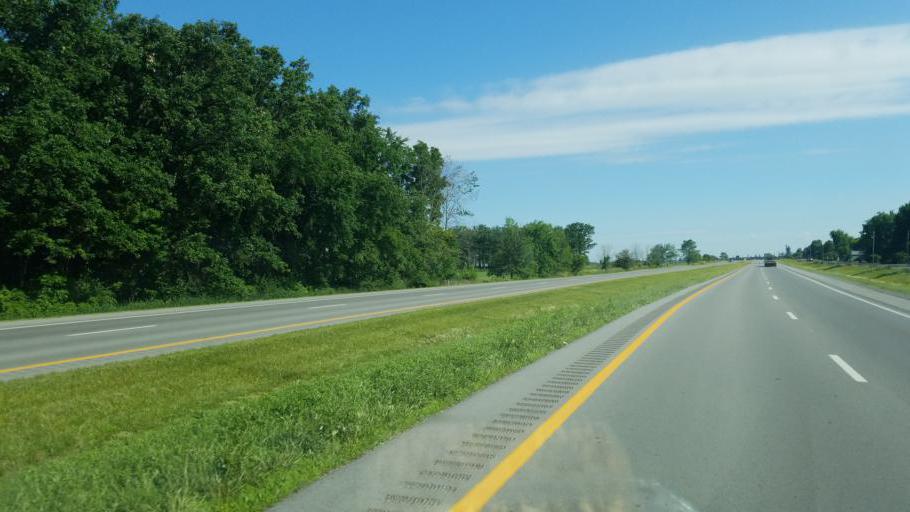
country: US
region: Ohio
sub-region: Hancock County
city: Findlay
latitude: 41.0049
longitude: -83.6604
